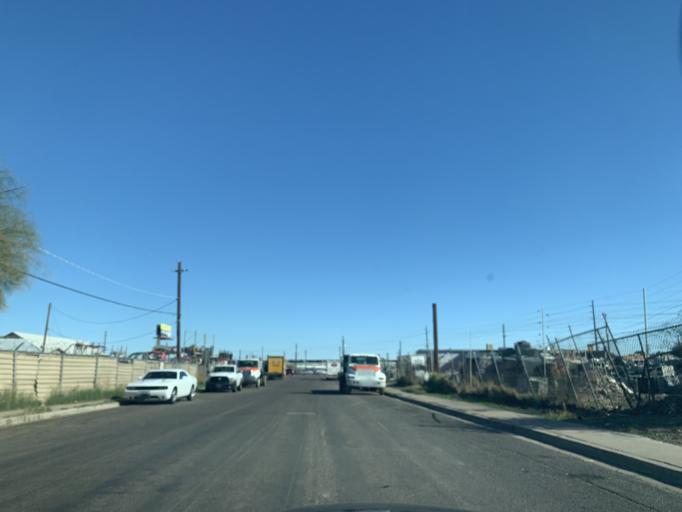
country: US
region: Arizona
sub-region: Maricopa County
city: Tempe Junction
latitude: 33.4164
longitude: -111.9969
